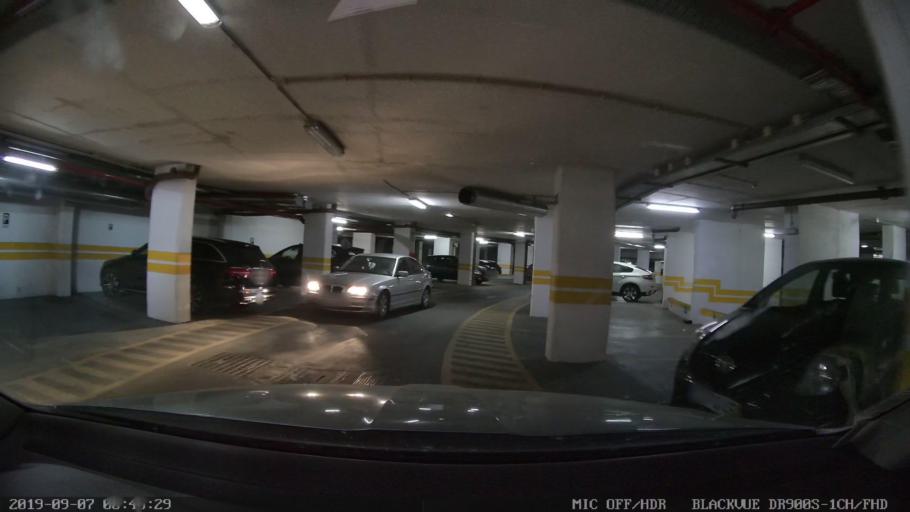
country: PT
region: Setubal
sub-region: Sesimbra
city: Sesimbra
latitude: 38.4419
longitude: -9.0954
